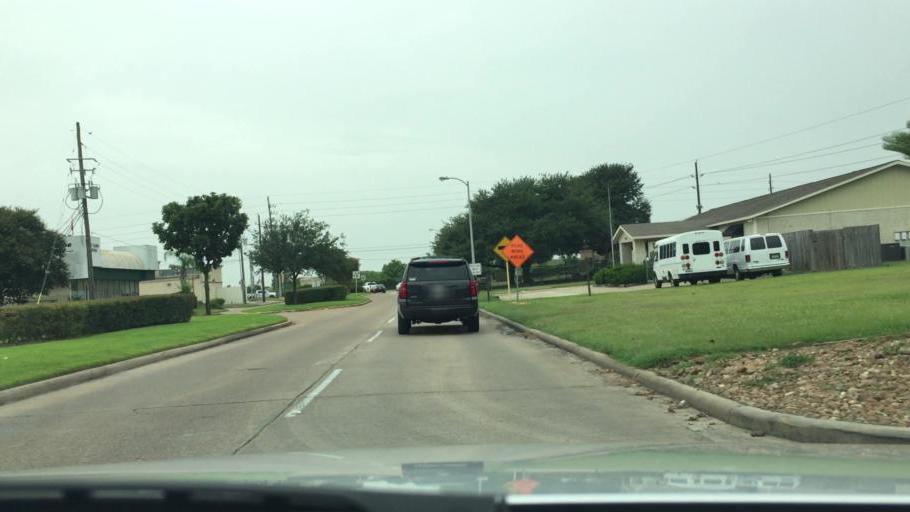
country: US
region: Texas
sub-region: Harris County
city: Hudson
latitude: 29.9025
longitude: -95.5220
